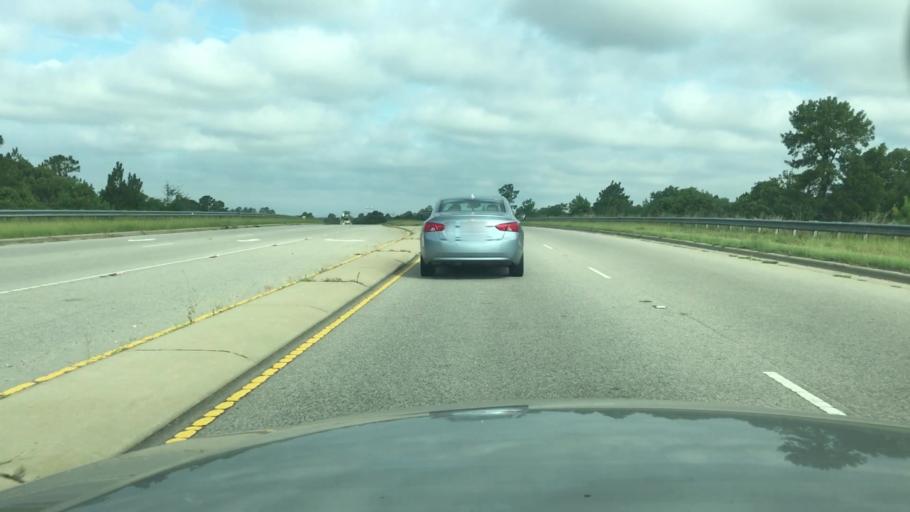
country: US
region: North Carolina
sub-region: Cumberland County
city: Hope Mills
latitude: 34.9893
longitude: -78.9375
